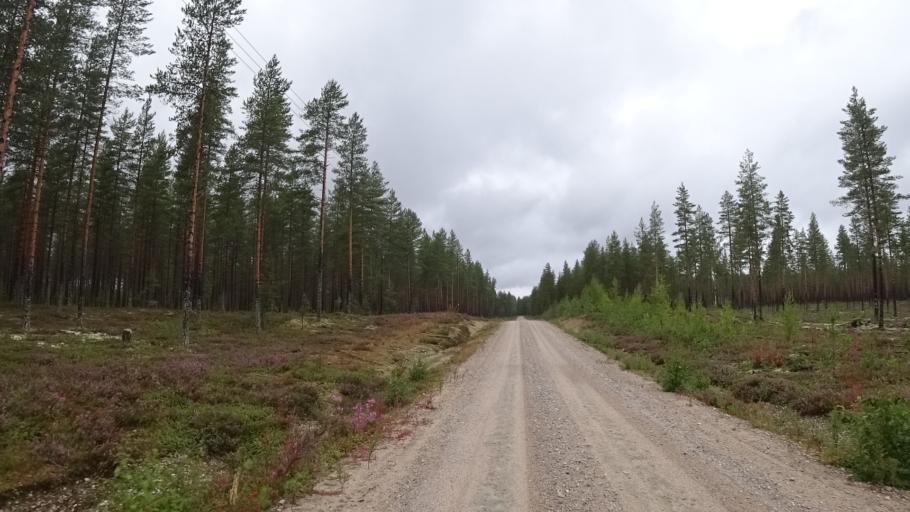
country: FI
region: North Karelia
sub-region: Pielisen Karjala
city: Lieksa
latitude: 63.5360
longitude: 30.0494
